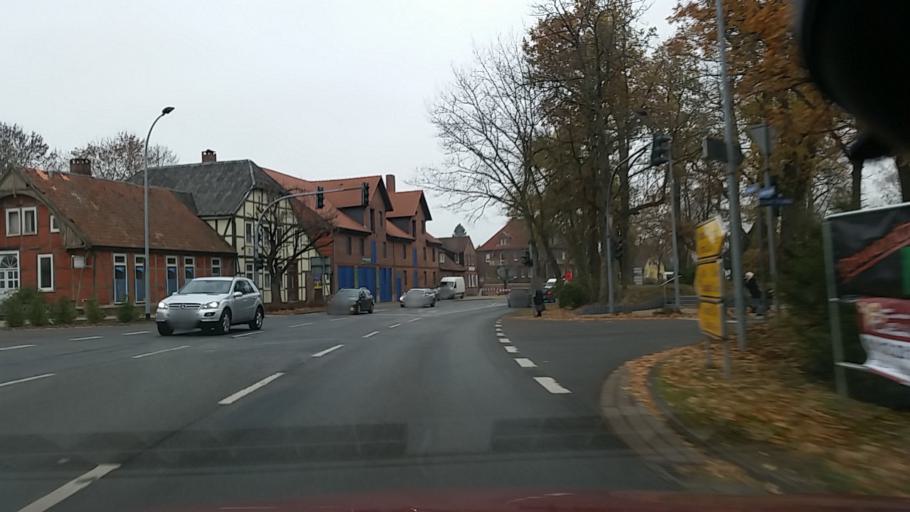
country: DE
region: Lower Saxony
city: Wittingen
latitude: 52.7270
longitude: 10.7381
